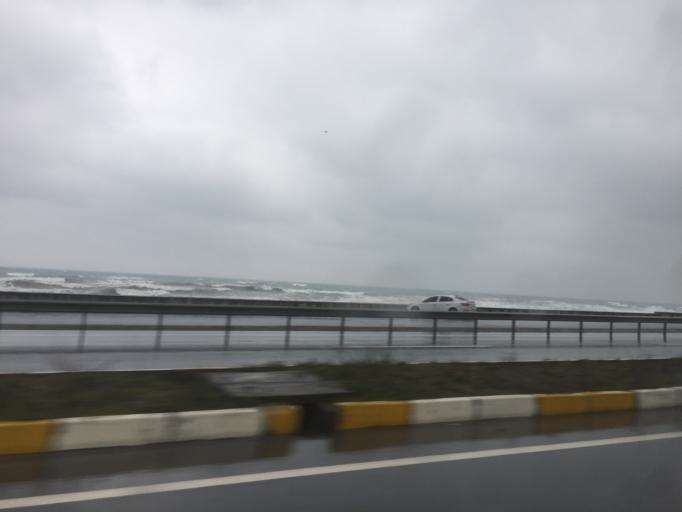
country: TR
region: Zonguldak
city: Alapli
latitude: 41.1074
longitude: 31.2637
